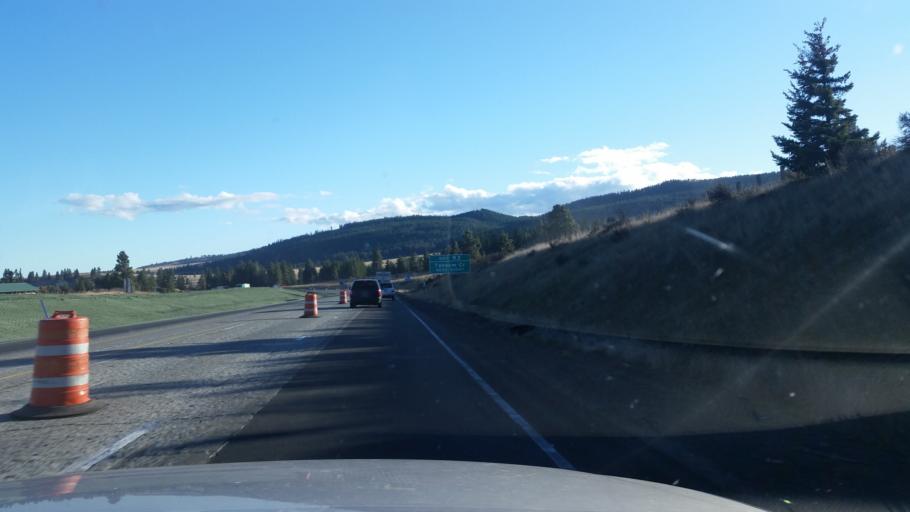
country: US
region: Washington
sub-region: Kittitas County
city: Cle Elum
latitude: 47.1212
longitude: -120.8009
